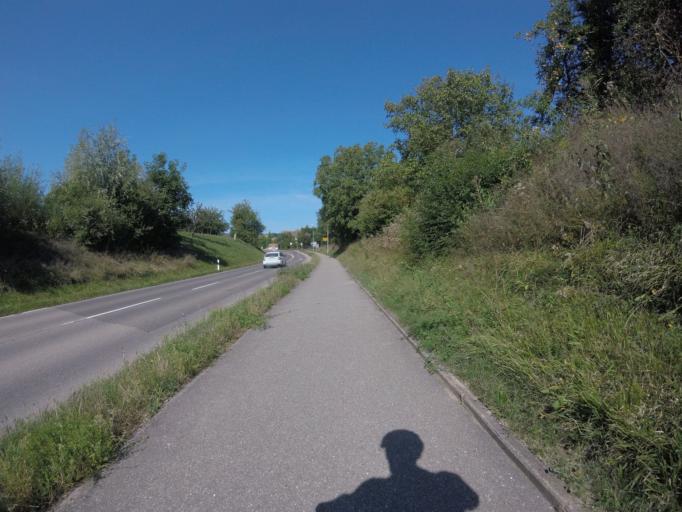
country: DE
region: Baden-Wuerttemberg
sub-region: Regierungsbezirk Stuttgart
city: Grossbottwar
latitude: 49.0202
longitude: 9.2655
